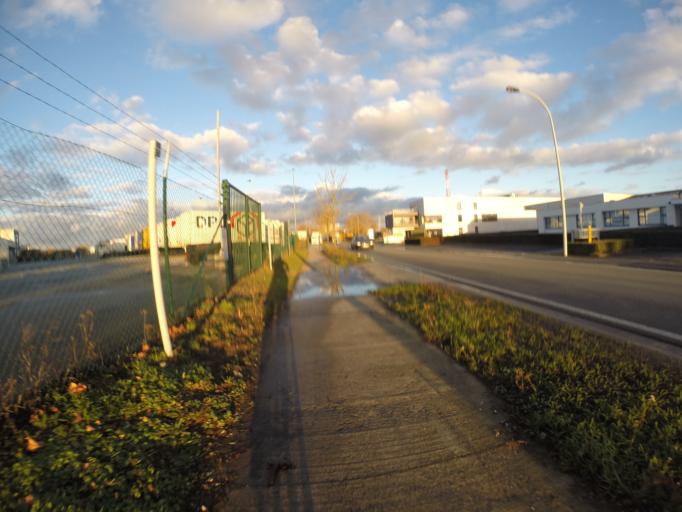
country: BE
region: Flanders
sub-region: Provincie Oost-Vlaanderen
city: Aalter
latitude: 51.1016
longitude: 3.4497
